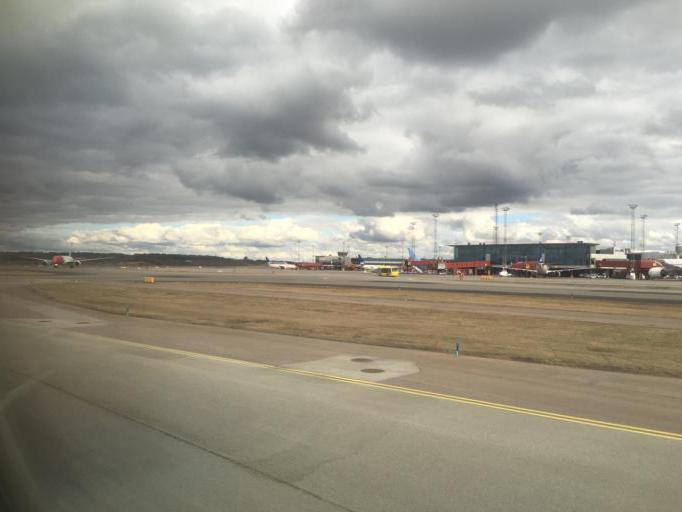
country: SE
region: Stockholm
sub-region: Sigtuna Kommun
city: Marsta
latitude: 59.6503
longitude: 17.9216
